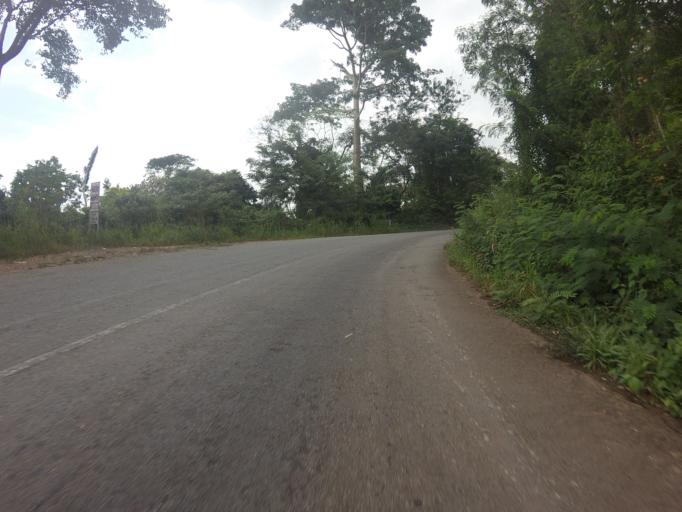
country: GH
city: Akropong
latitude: 5.9600
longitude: -0.1188
